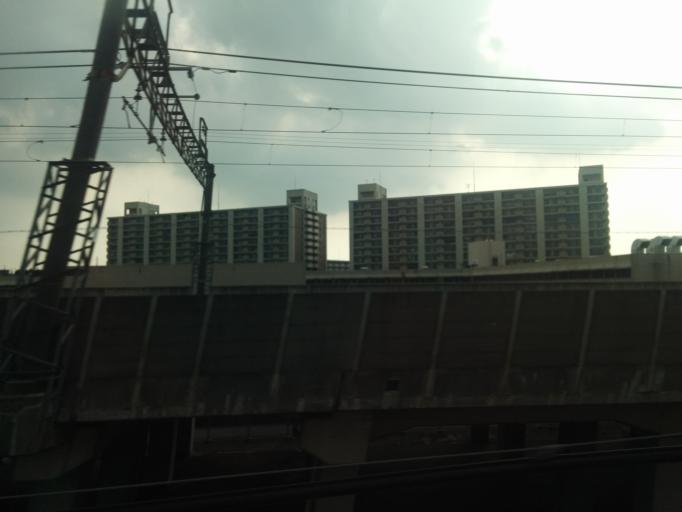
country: JP
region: Aichi
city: Obu
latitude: 35.0625
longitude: 136.9444
